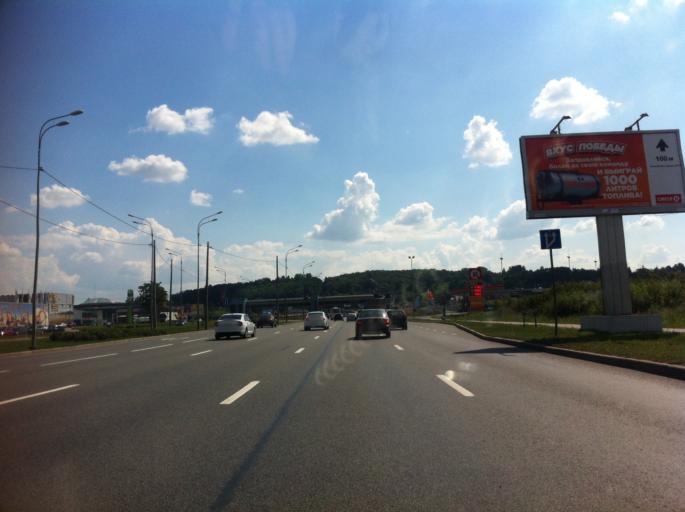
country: RU
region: St.-Petersburg
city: Aleksandrovskaya
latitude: 59.7833
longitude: 30.3249
